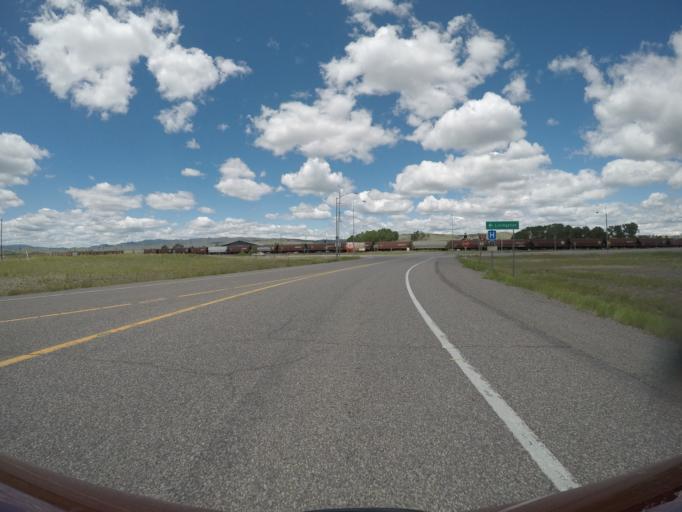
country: US
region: Montana
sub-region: Park County
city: Livingston
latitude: 45.6873
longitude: -110.5034
